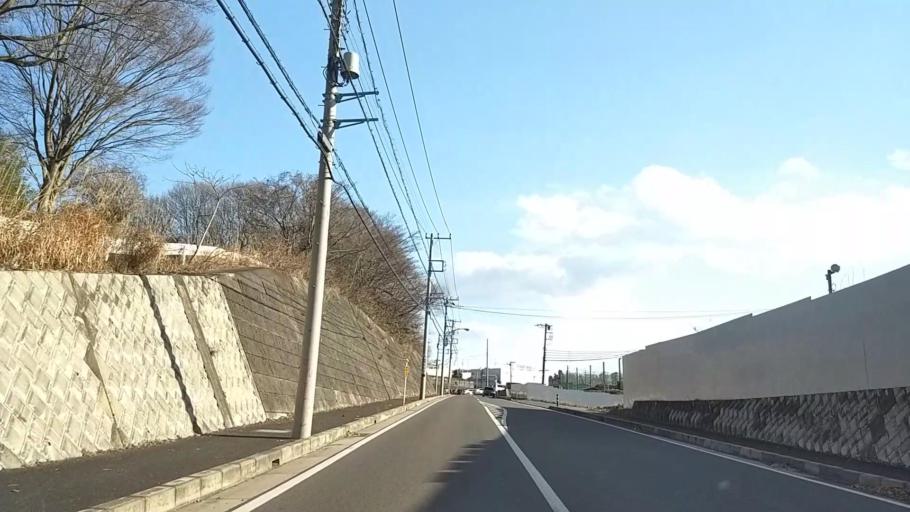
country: JP
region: Kanagawa
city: Atsugi
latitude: 35.4586
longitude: 139.3137
